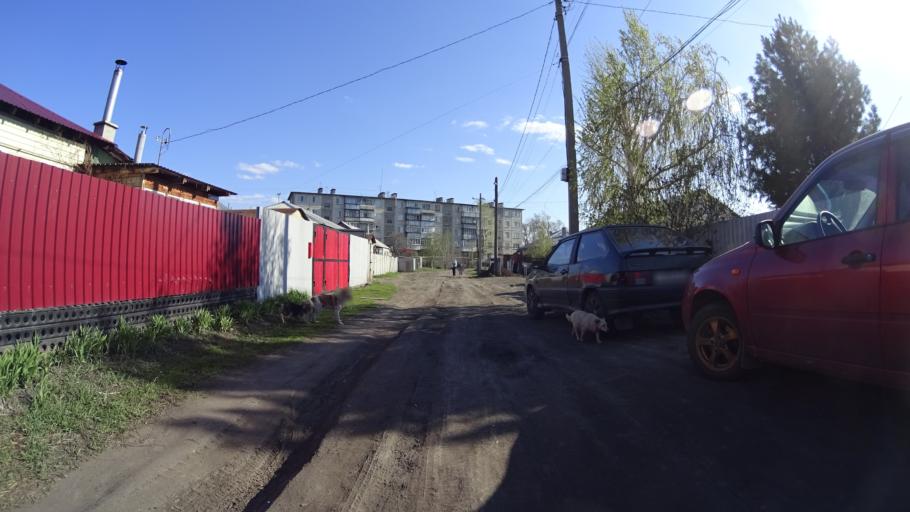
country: RU
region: Chelyabinsk
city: Troitsk
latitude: 54.1062
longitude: 61.5571
